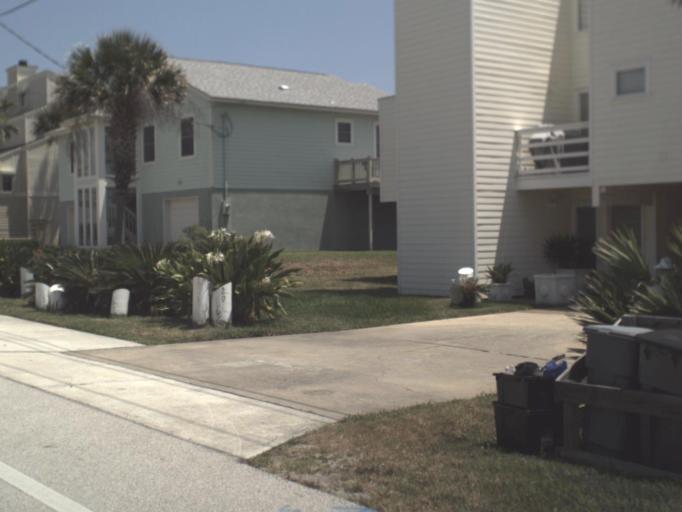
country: US
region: Florida
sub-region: Saint Johns County
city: Villano Beach
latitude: 29.9961
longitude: -81.3167
